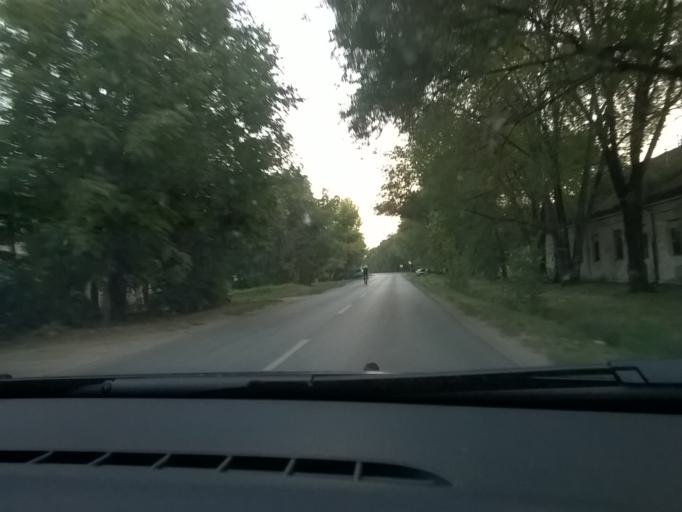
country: RS
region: Autonomna Pokrajina Vojvodina
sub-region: Juznobanatski Okrug
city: Vrsac
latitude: 45.1088
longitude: 21.2980
